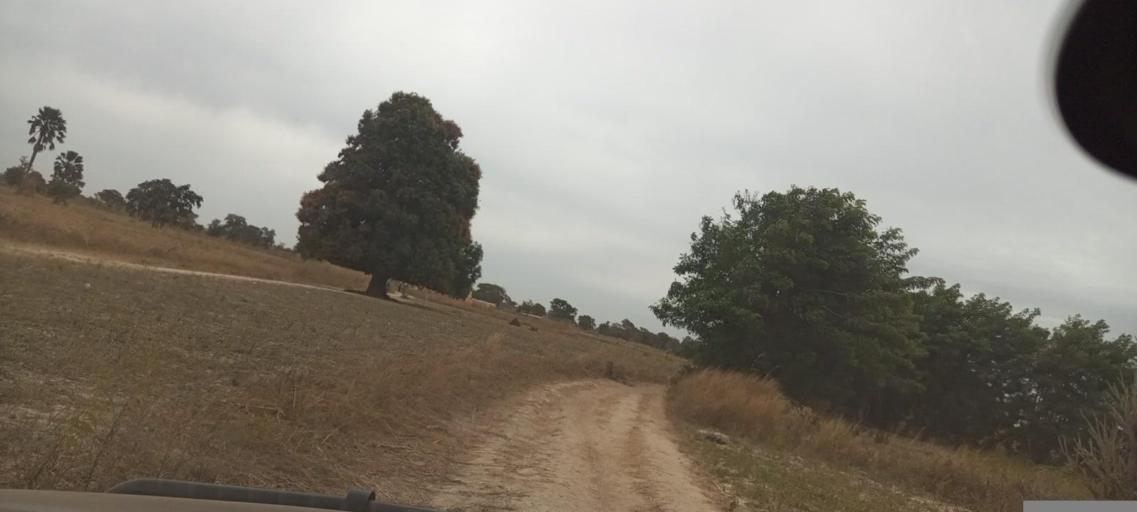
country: ML
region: Koulikoro
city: Kati
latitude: 12.7535
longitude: -8.3121
